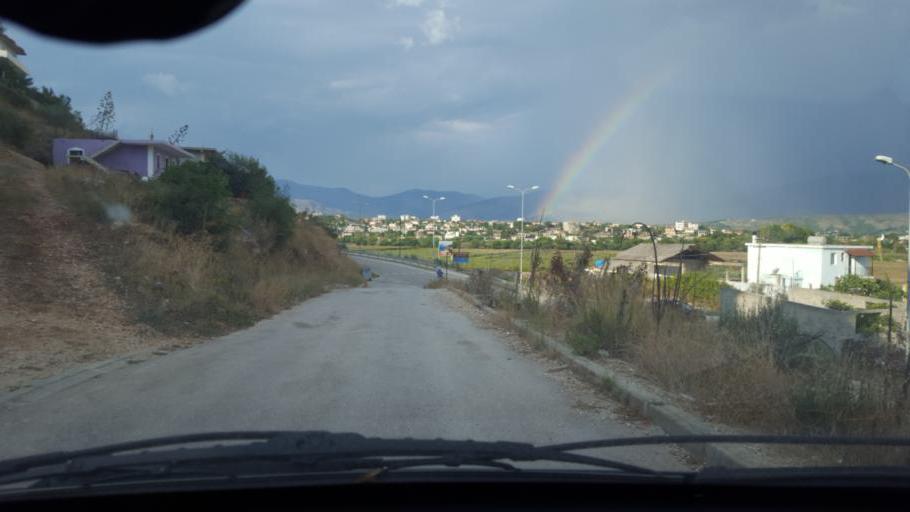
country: AL
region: Vlore
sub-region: Rrethi i Sarandes
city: Sarande
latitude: 39.8398
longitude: 20.0240
